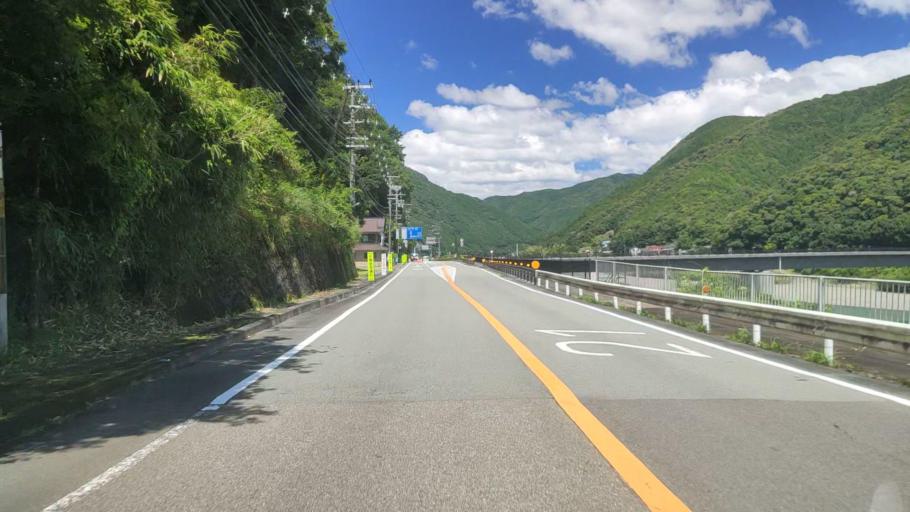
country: JP
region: Wakayama
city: Shingu
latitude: 33.8328
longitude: 135.8541
